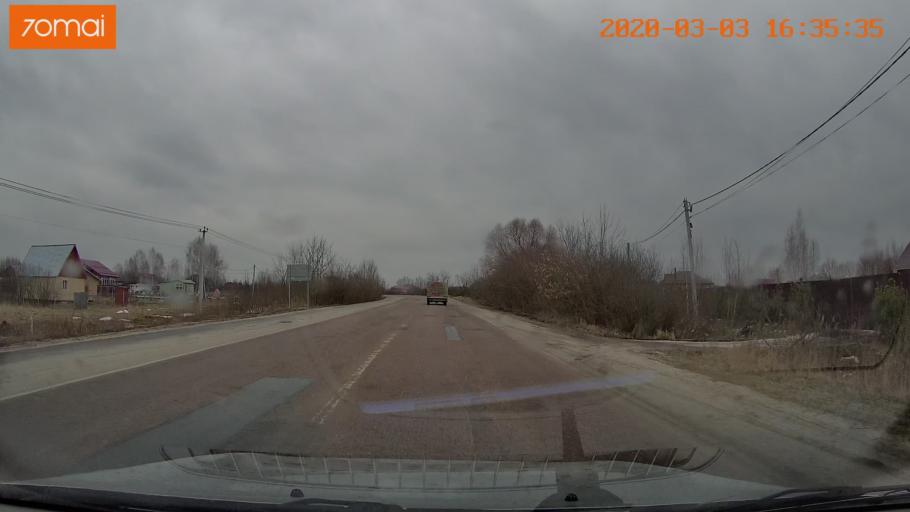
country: RU
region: Moskovskaya
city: Lopatinskiy
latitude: 55.4036
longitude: 38.7651
